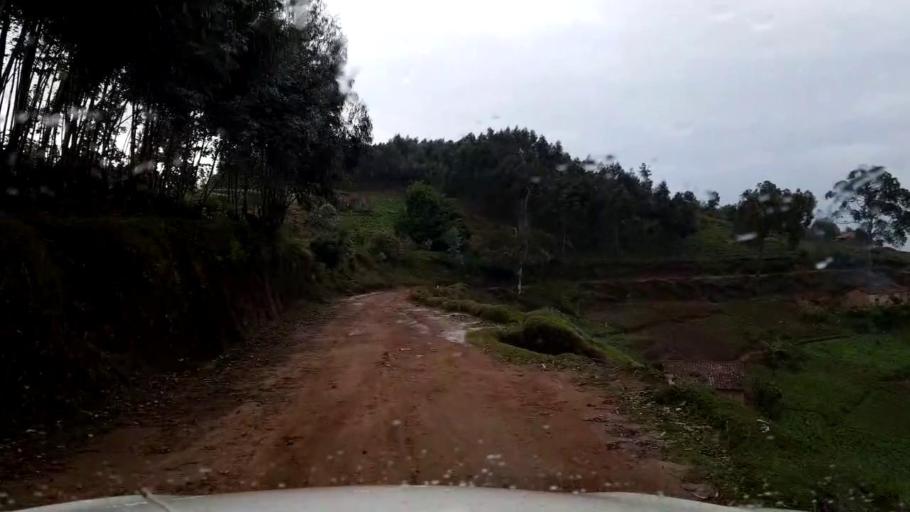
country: RW
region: Western Province
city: Kibuye
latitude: -2.0187
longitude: 29.4648
